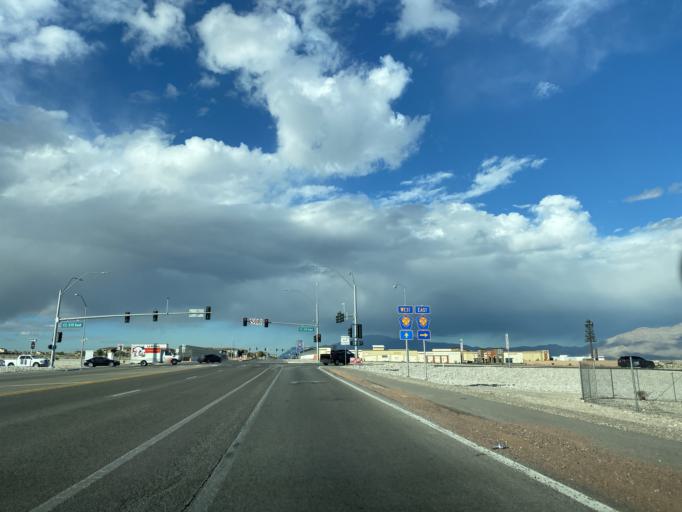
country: US
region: Nevada
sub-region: Clark County
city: Summerlin South
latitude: 36.2798
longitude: -115.3149
